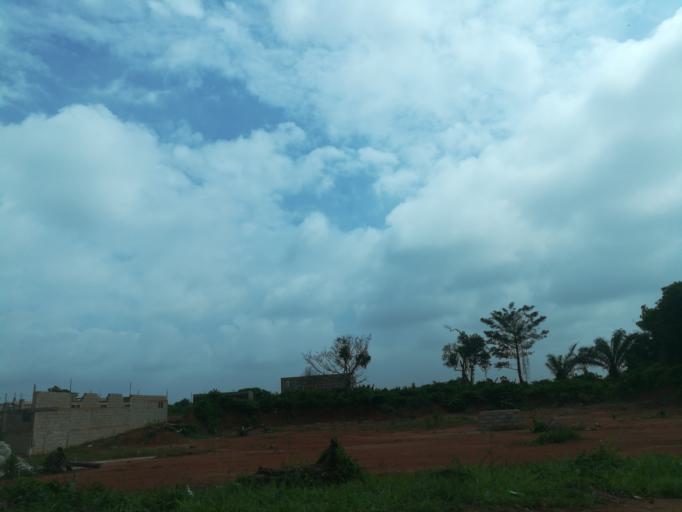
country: NG
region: Lagos
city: Ikorodu
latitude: 6.6722
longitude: 3.6605
